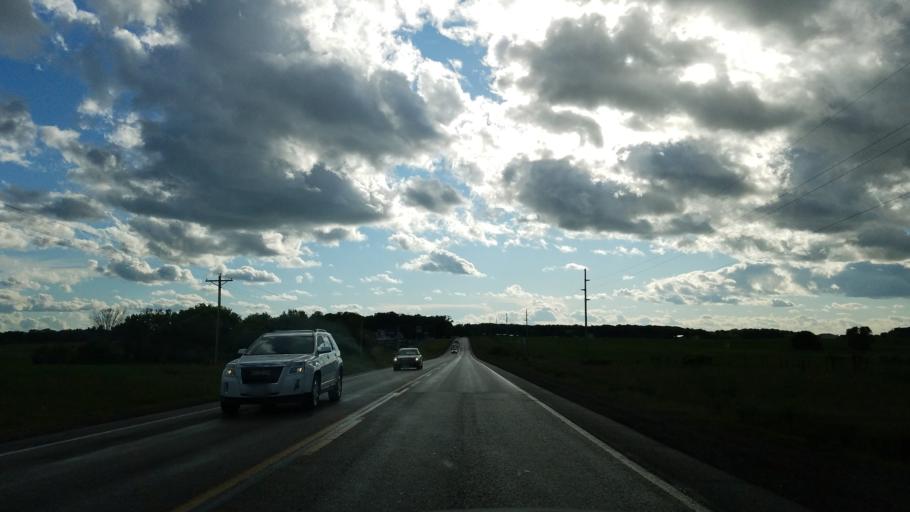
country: US
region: Wisconsin
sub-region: Polk County
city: Osceola
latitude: 45.3433
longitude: -92.6551
